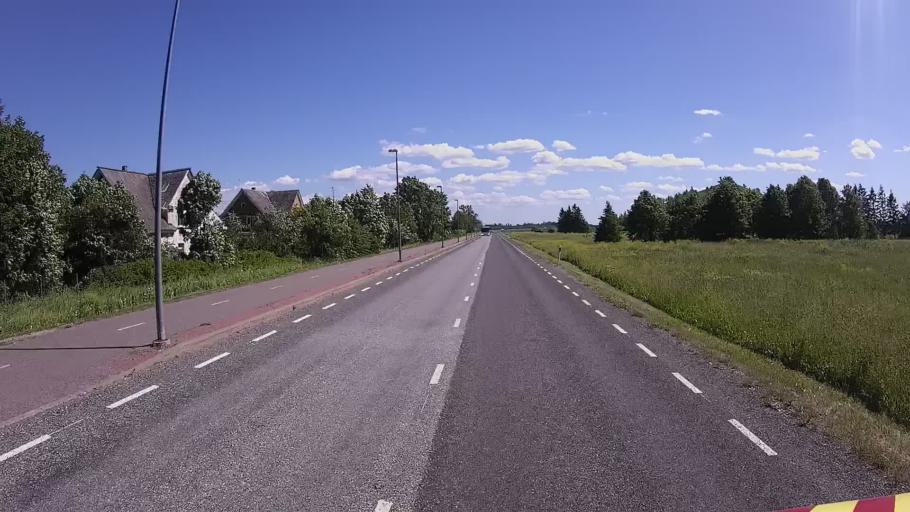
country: EE
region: Ida-Virumaa
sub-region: Kohtla-Jaerve linn
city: Kohtla-Jarve
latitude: 59.3988
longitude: 27.3401
